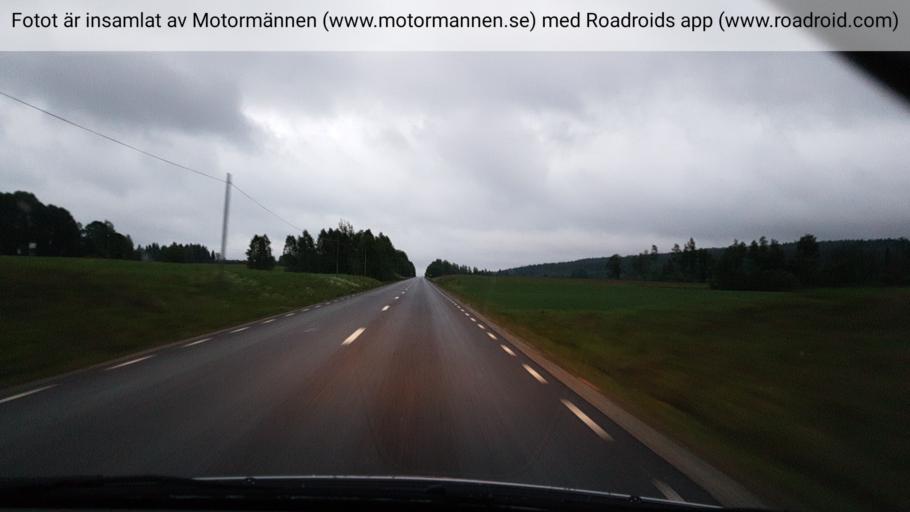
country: SE
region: Vaestmanland
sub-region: Skinnskattebergs Kommun
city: Skinnskatteberg
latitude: 59.9046
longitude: 15.5472
